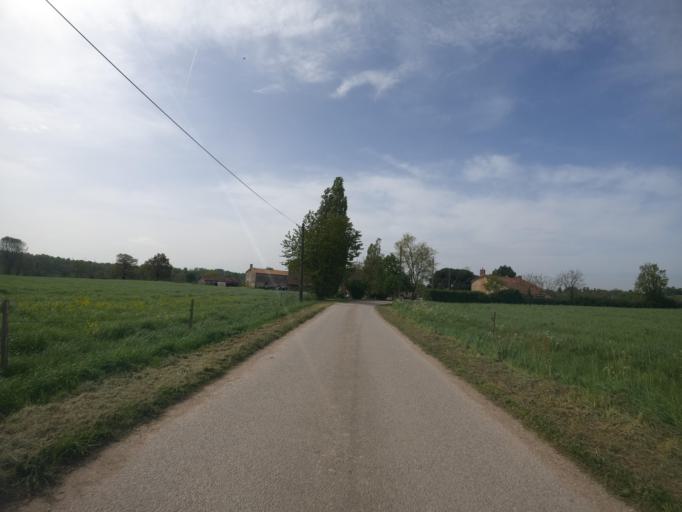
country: FR
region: Poitou-Charentes
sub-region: Departement des Deux-Sevres
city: La Chapelle-Saint-Laurent
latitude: 46.7030
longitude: -0.5064
